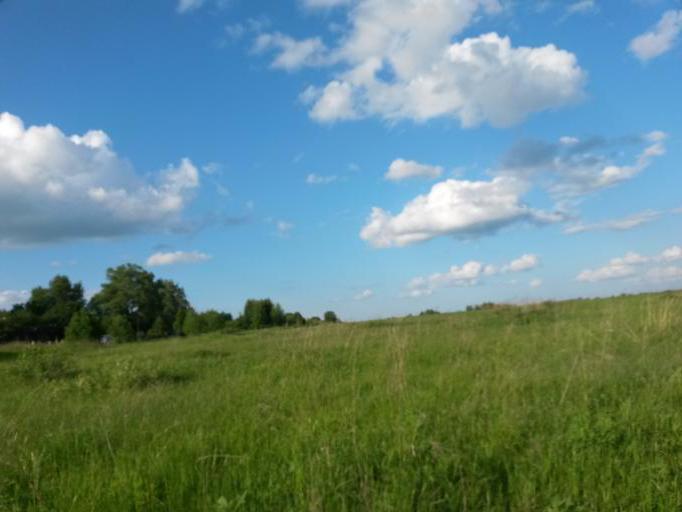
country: RU
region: Jaroslavl
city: Burmakino
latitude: 57.3599
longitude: 40.1994
